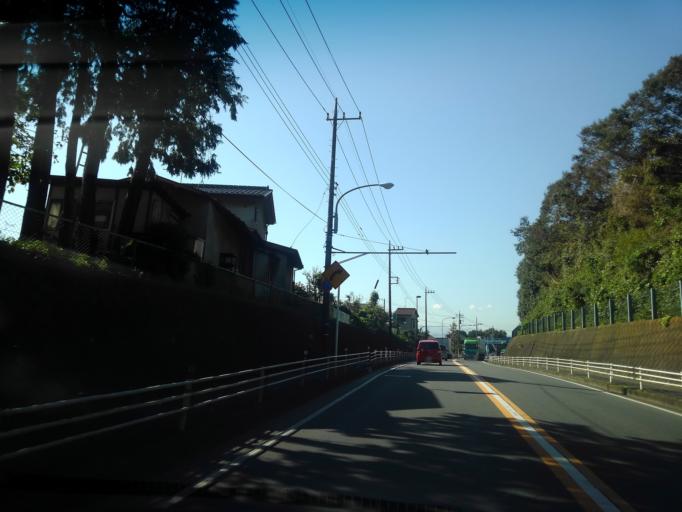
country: JP
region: Tokyo
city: Fussa
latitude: 35.7769
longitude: 139.3521
